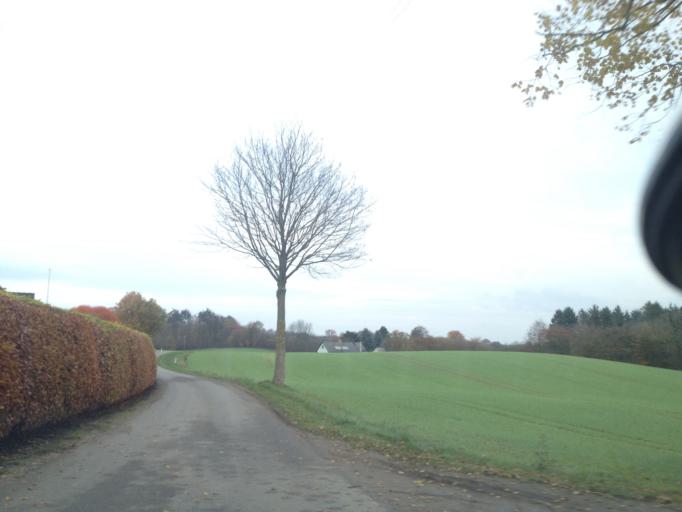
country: DK
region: South Denmark
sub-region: Assens Kommune
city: Vissenbjerg
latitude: 55.4213
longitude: 10.1642
